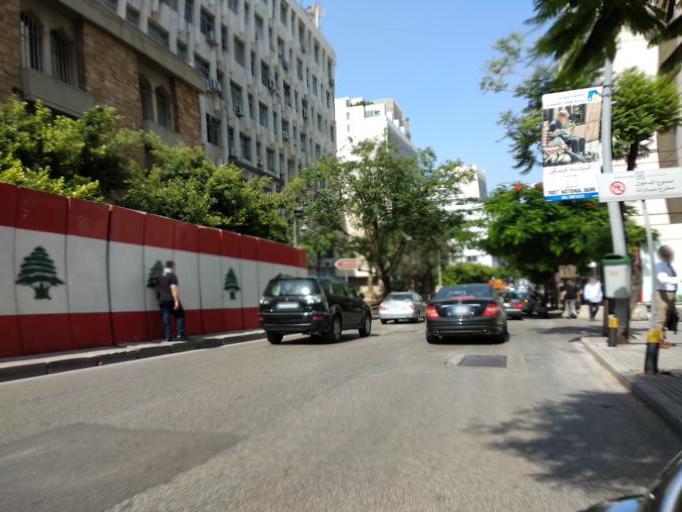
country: LB
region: Beyrouth
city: Ra's Bayrut
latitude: 33.8954
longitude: 35.4887
